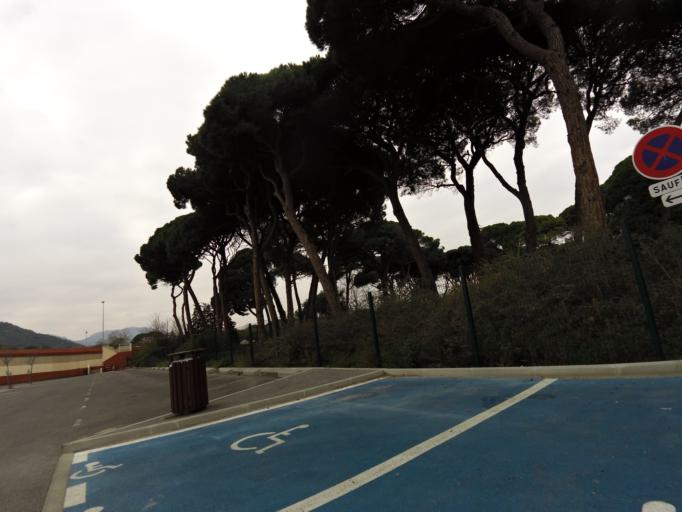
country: FR
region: Provence-Alpes-Cote d'Azur
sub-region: Departement des Alpes-Maritimes
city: Mandelieu-la-Napoule
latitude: 43.5321
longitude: 6.9485
